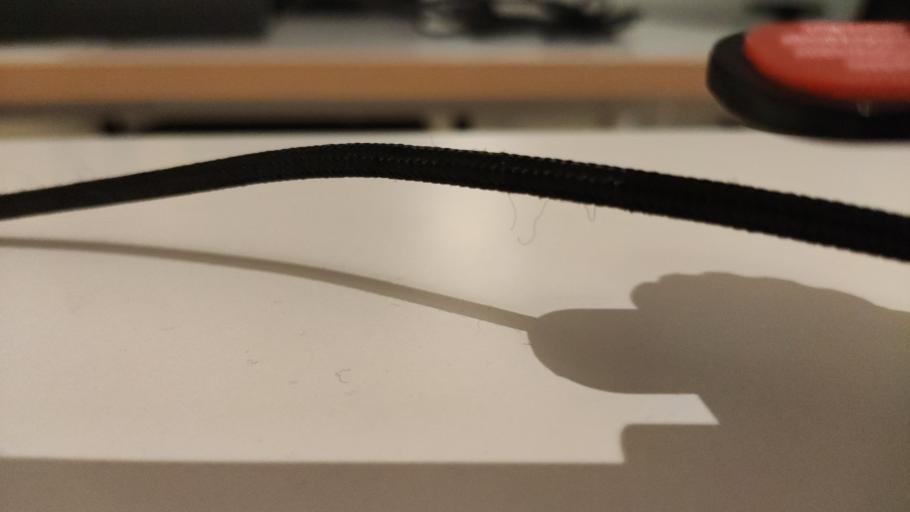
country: RU
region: Moskovskaya
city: Skoropuskovskiy
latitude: 56.3756
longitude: 38.1068
